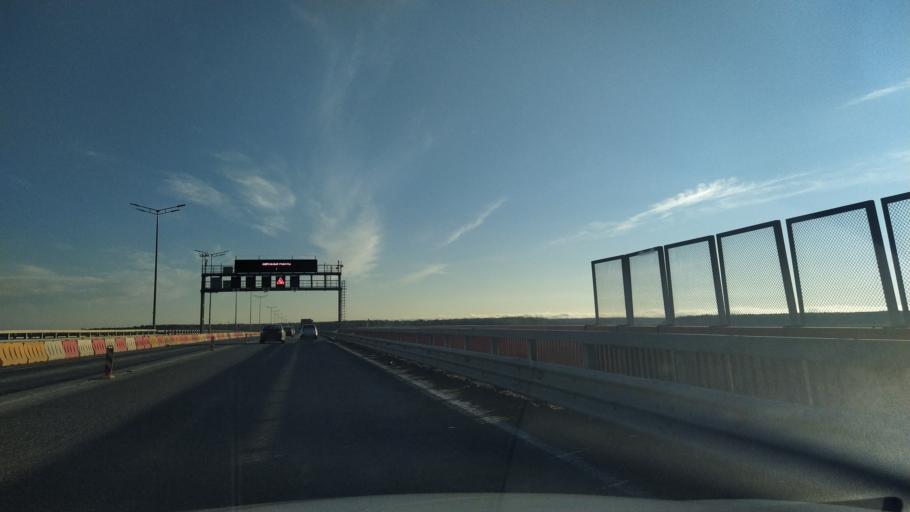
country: RU
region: St.-Petersburg
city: Pargolovo
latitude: 60.0921
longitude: 30.2451
